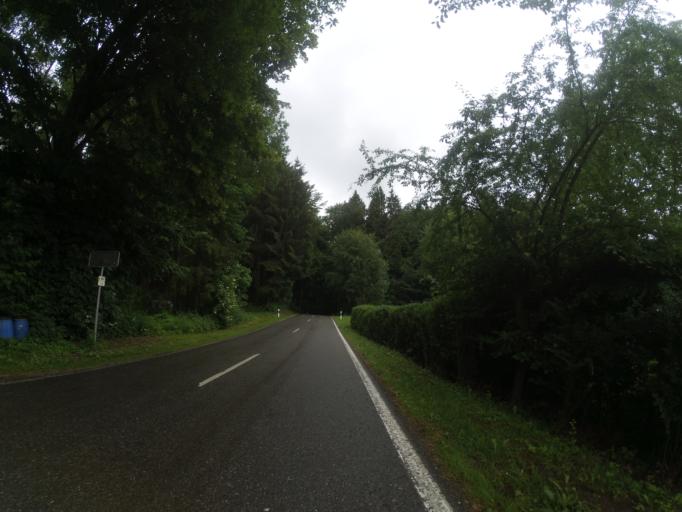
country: DE
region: Baden-Wuerttemberg
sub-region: Tuebingen Region
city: Wangen im Allgau
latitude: 47.7361
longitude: 9.8440
